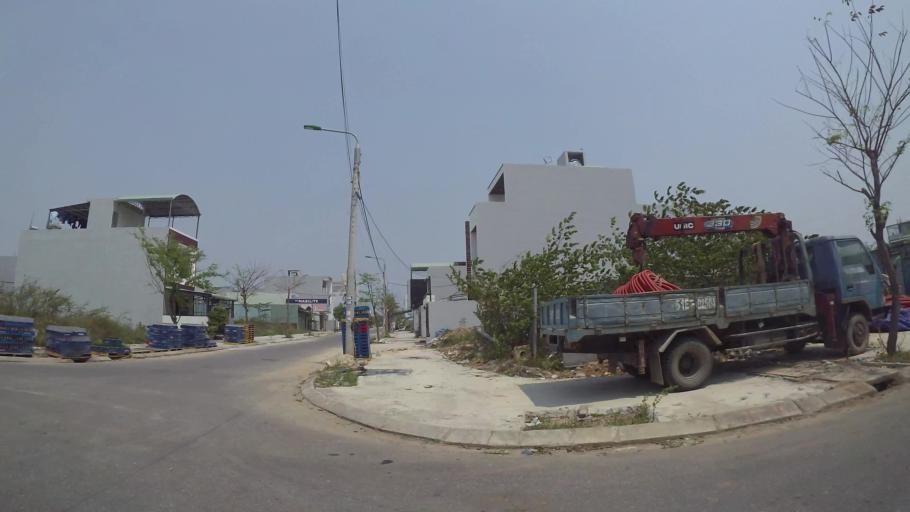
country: VN
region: Da Nang
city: Cam Le
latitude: 16.0110
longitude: 108.2213
